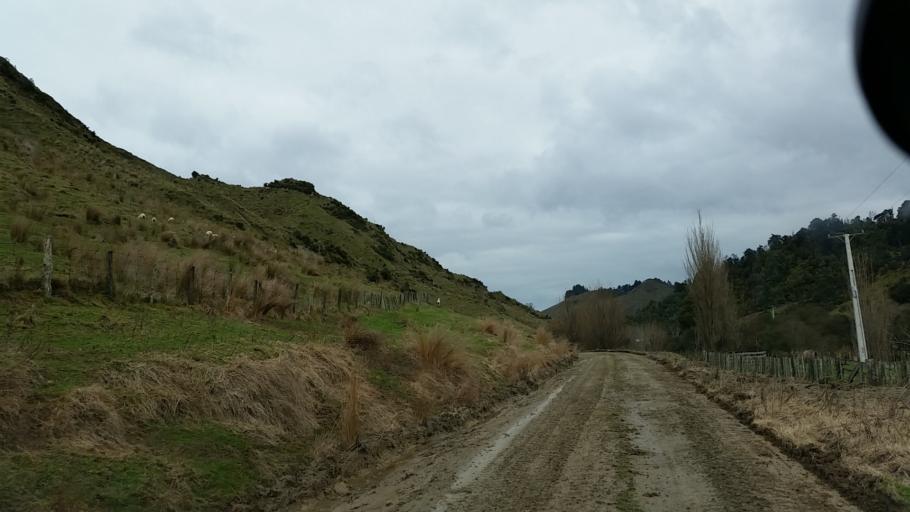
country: NZ
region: Taranaki
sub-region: South Taranaki District
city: Patea
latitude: -39.6492
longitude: 174.7554
